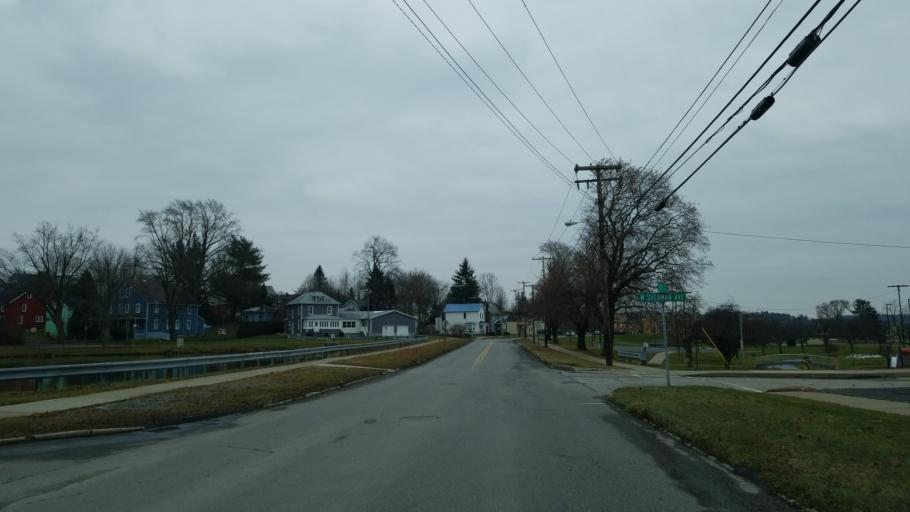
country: US
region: Pennsylvania
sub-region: Clearfield County
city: DuBois
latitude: 41.1321
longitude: -78.7575
